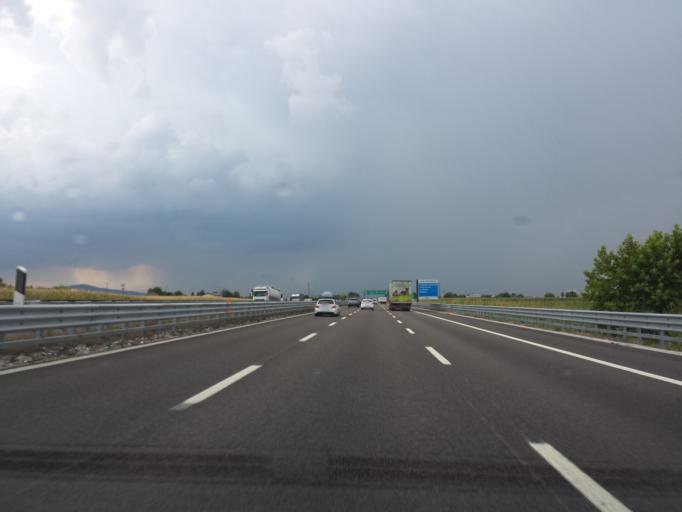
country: IT
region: Veneto
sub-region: Provincia di Padova
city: Arlesega
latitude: 45.4751
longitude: 11.7170
